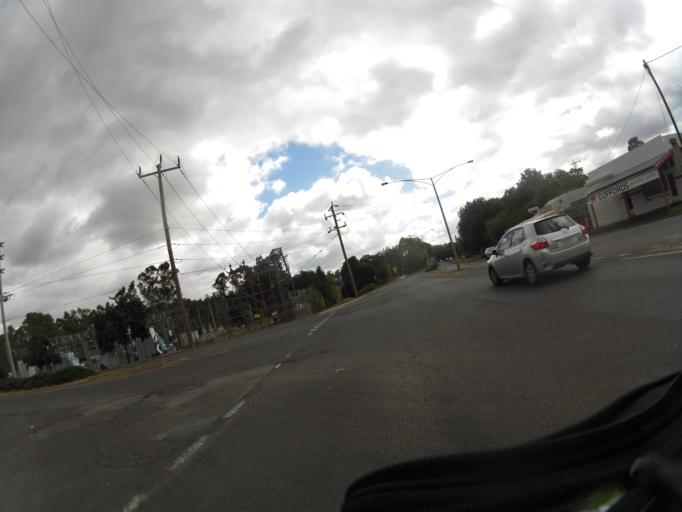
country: AU
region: Victoria
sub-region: Mount Alexander
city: Castlemaine
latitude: -37.0730
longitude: 144.2067
